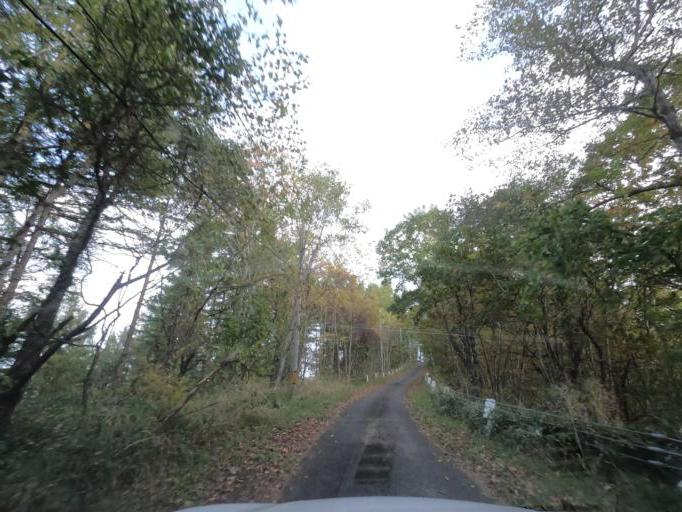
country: JP
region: Hokkaido
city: Obihiro
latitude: 42.5848
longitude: 143.3130
